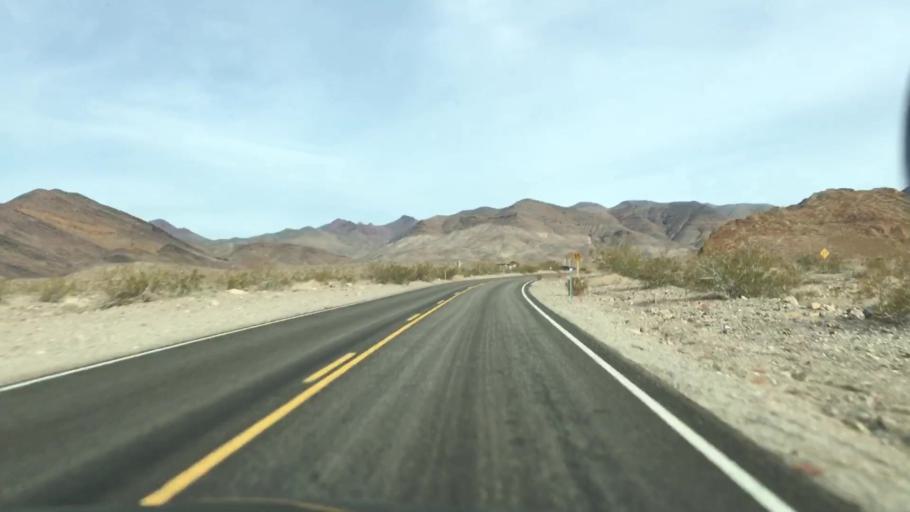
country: US
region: Nevada
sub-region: Nye County
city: Beatty
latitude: 36.7219
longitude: -116.9789
